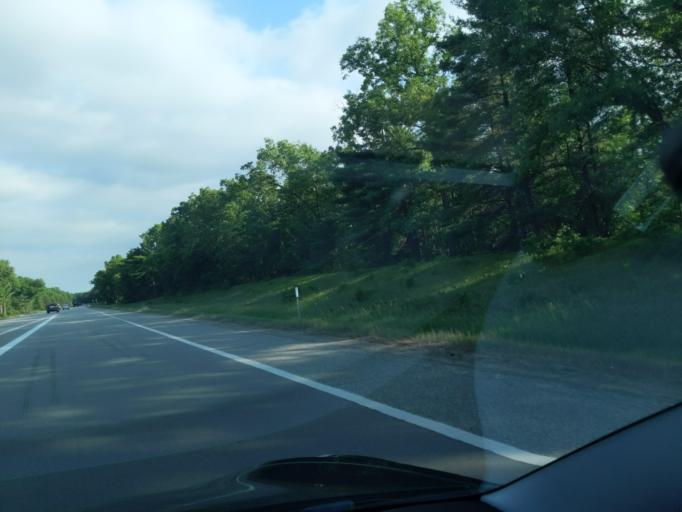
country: US
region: Michigan
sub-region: Muskegon County
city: Lakewood Club
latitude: 43.3807
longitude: -86.2796
